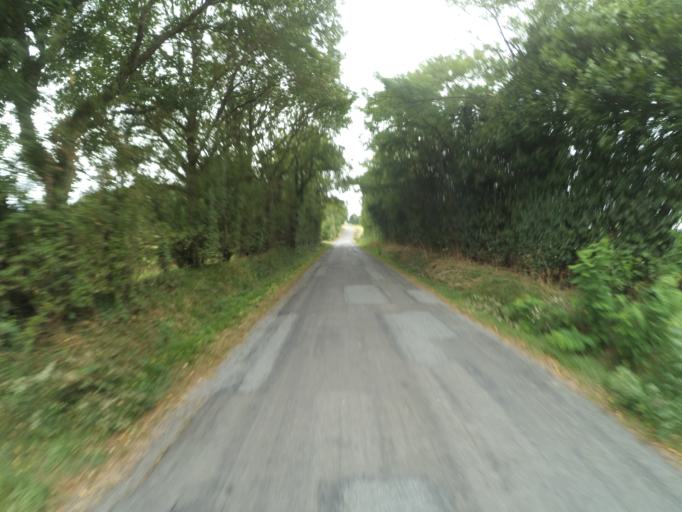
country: FR
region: Pays de la Loire
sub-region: Departement de la Vendee
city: Saint-Philbert-de-Bouaine
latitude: 47.0165
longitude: -1.5519
